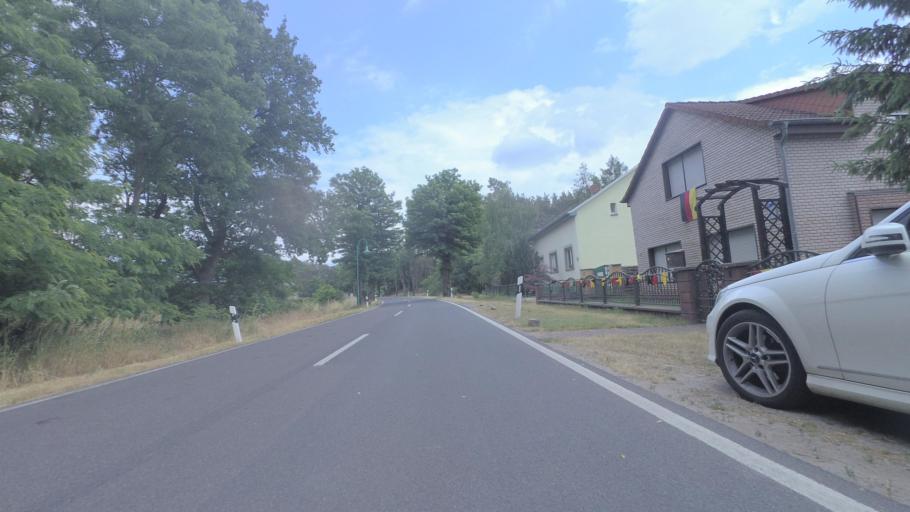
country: DE
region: Brandenburg
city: Am Mellensee
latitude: 52.1334
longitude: 13.4608
